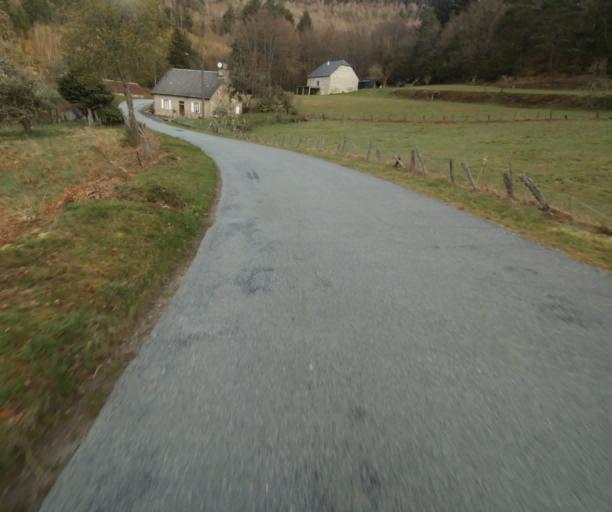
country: FR
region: Limousin
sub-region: Departement de la Correze
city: Correze
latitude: 45.4194
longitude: 1.8976
